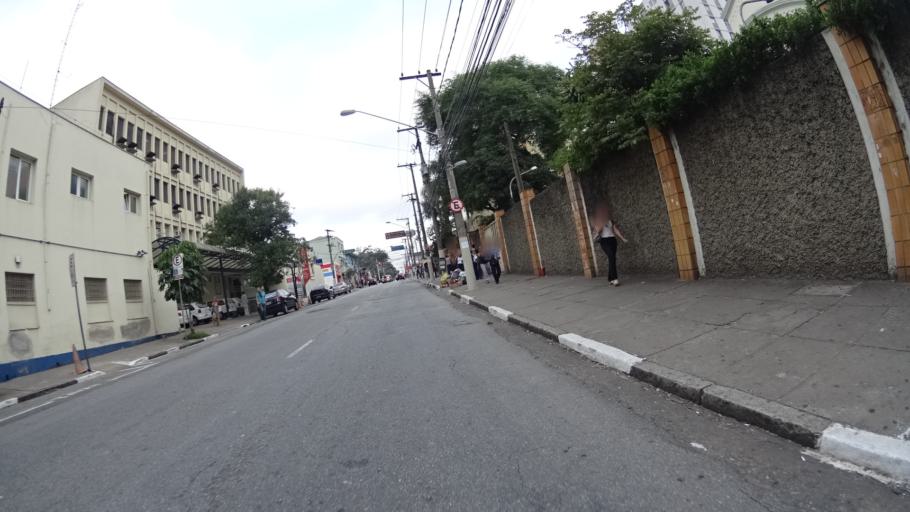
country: BR
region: Sao Paulo
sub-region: Sao Paulo
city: Sao Paulo
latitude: -23.5970
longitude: -46.6361
